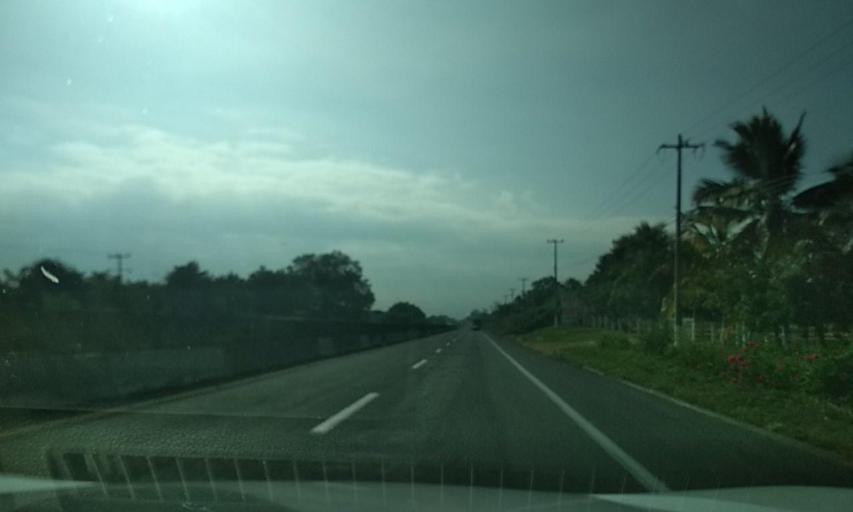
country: MX
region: Veracruz
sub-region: Emiliano Zapata
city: Plan del Rio
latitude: 19.3904
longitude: -96.6093
